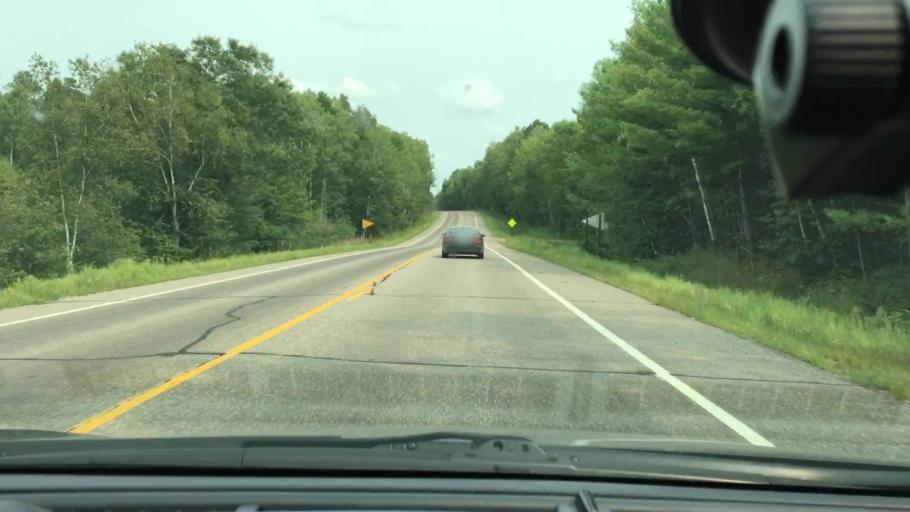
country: US
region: Minnesota
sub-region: Crow Wing County
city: Cross Lake
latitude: 46.7310
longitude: -94.0082
